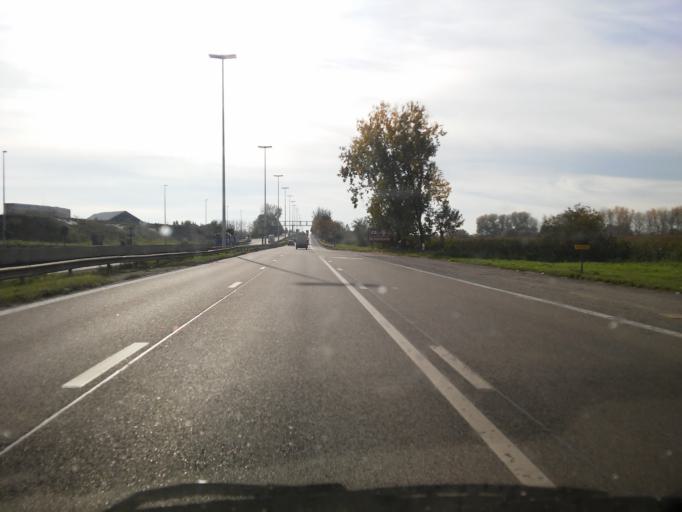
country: BE
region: Flanders
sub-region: Provincie Antwerpen
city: Willebroek
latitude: 51.0722
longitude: 4.3454
